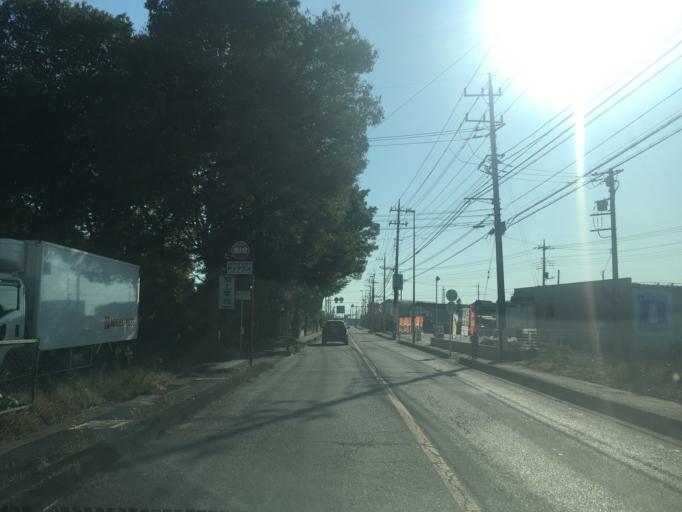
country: JP
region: Saitama
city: Tokorozawa
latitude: 35.8382
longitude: 139.4661
